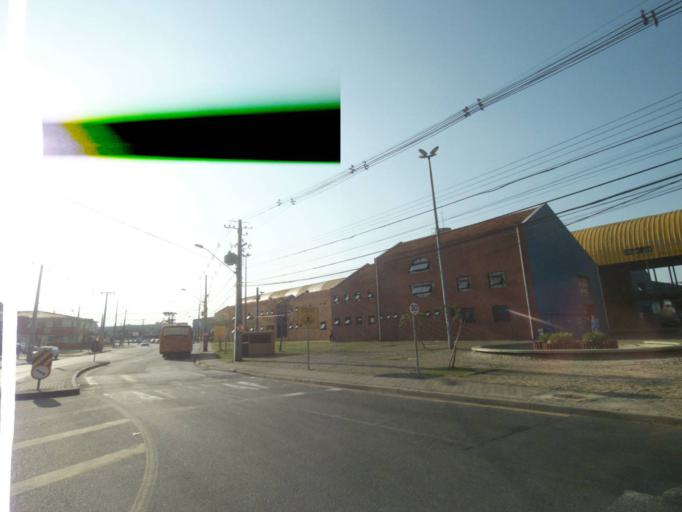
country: BR
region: Parana
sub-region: Curitiba
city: Curitiba
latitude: -25.4785
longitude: -49.3268
